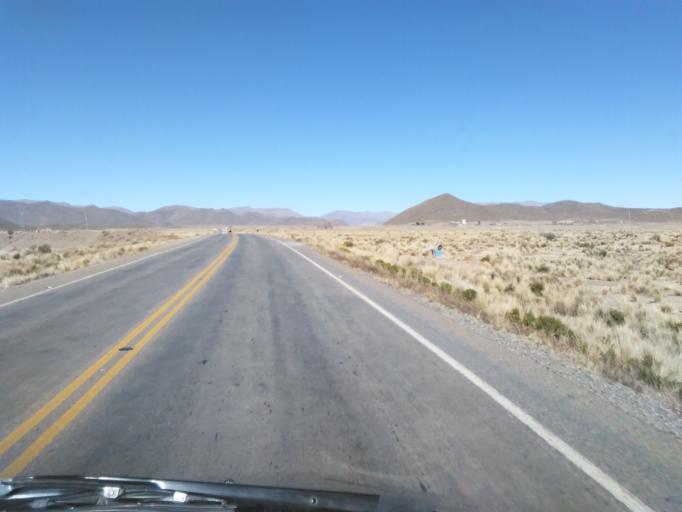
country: BO
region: Oruro
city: Machacamarca
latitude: -18.1592
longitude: -66.9708
